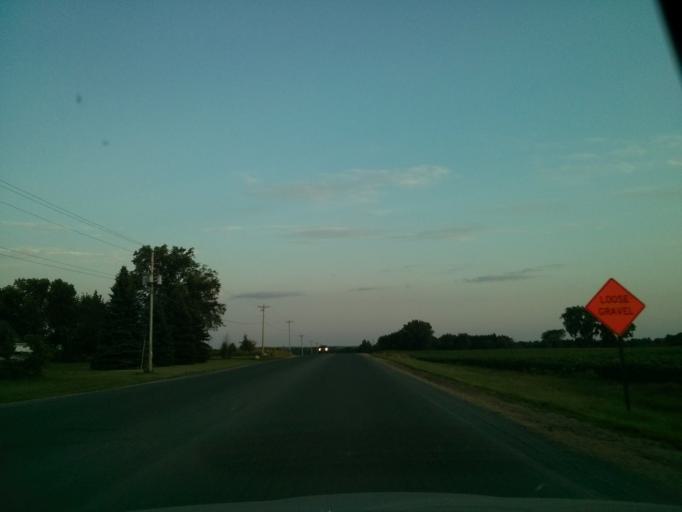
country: US
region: Wisconsin
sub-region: Saint Croix County
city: North Hudson
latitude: 45.0025
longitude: -92.6755
